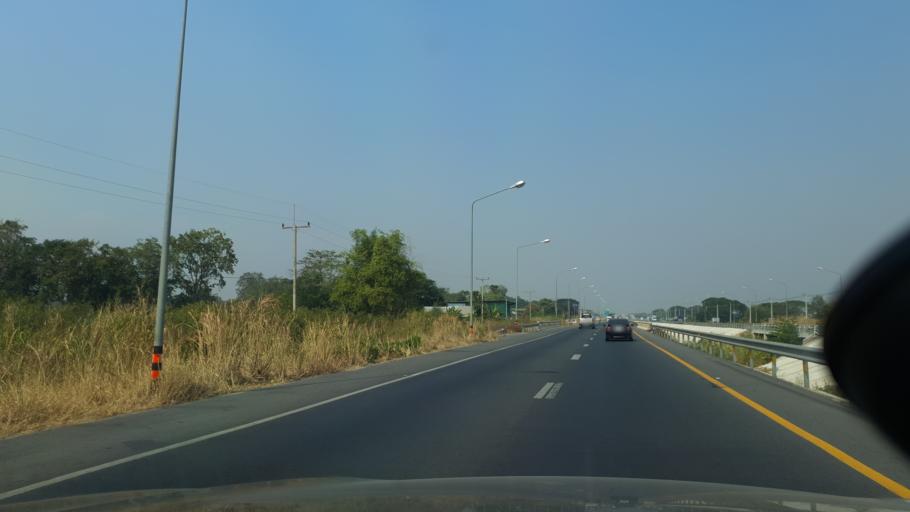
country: TH
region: Nakhon Sawan
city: Krok Phra
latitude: 15.6257
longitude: 100.1099
